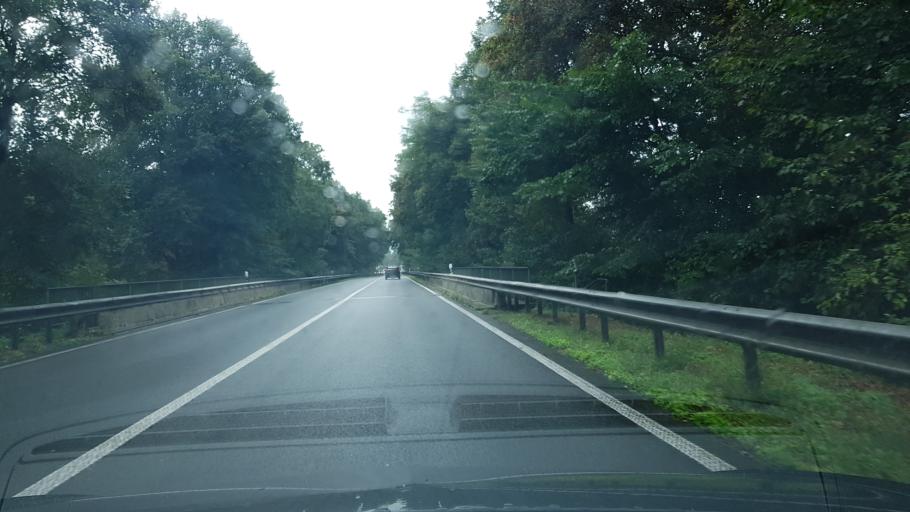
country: DE
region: North Rhine-Westphalia
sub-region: Regierungsbezirk Dusseldorf
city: Nettetal
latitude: 51.3094
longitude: 6.2175
